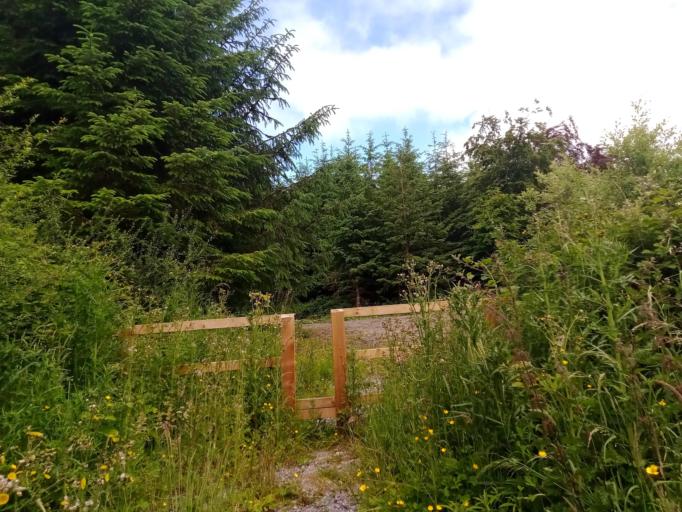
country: IE
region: Leinster
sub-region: Kilkenny
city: Ballyragget
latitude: 52.7874
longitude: -7.4471
